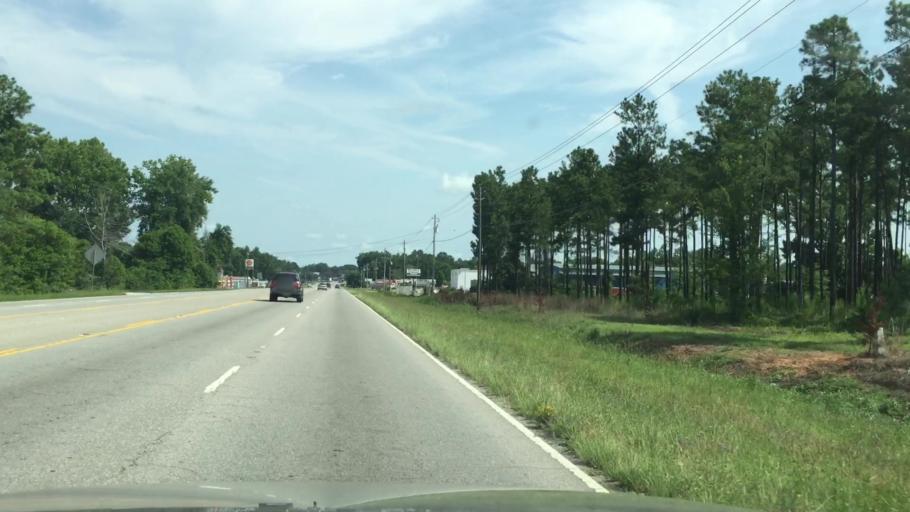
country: US
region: South Carolina
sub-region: Sumter County
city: South Sumter
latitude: 33.8922
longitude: -80.3516
